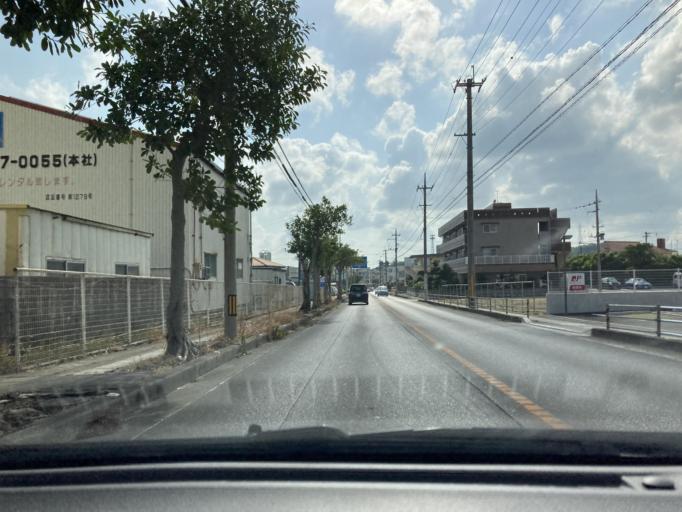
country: JP
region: Okinawa
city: Tomigusuku
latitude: 26.1566
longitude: 127.7251
